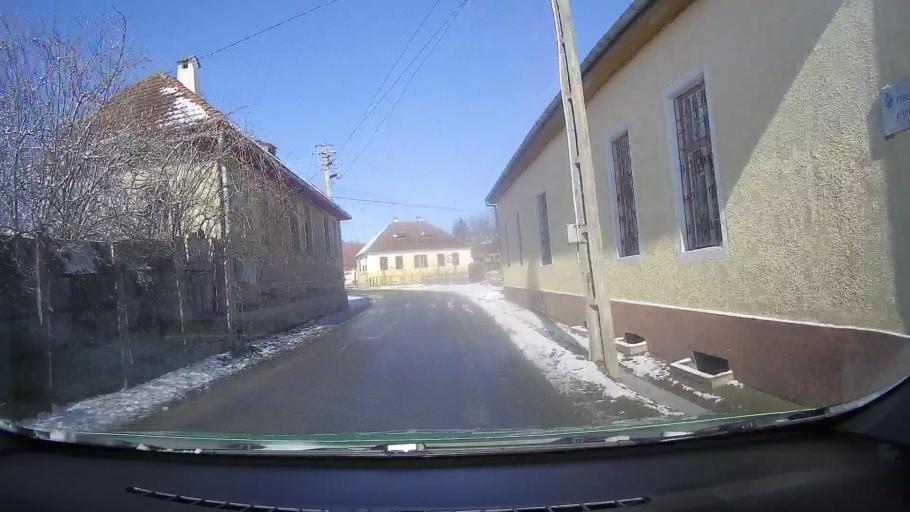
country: RO
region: Sibiu
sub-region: Comuna Avrig
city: Avrig
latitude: 45.7606
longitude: 24.3897
